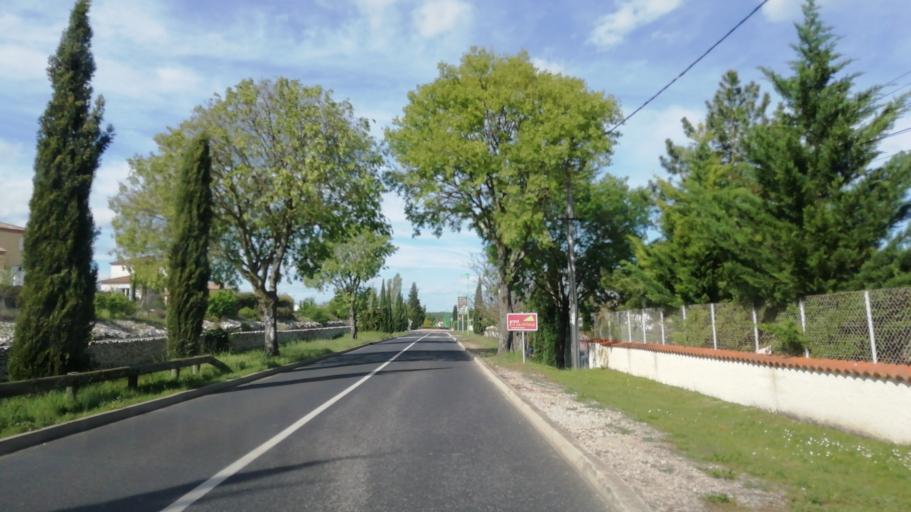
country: FR
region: Languedoc-Roussillon
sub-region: Departement de l'Herault
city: Saint-Martin-de-Londres
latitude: 43.7818
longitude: 3.7259
